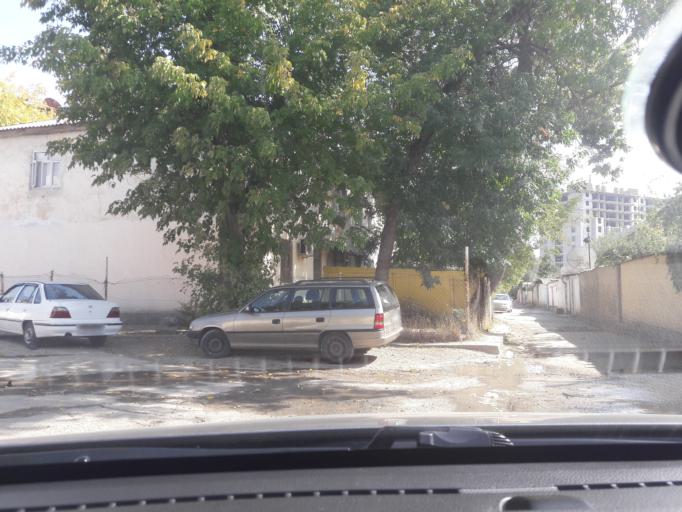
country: TJ
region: Dushanbe
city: Dushanbe
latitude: 38.5772
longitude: 68.7990
